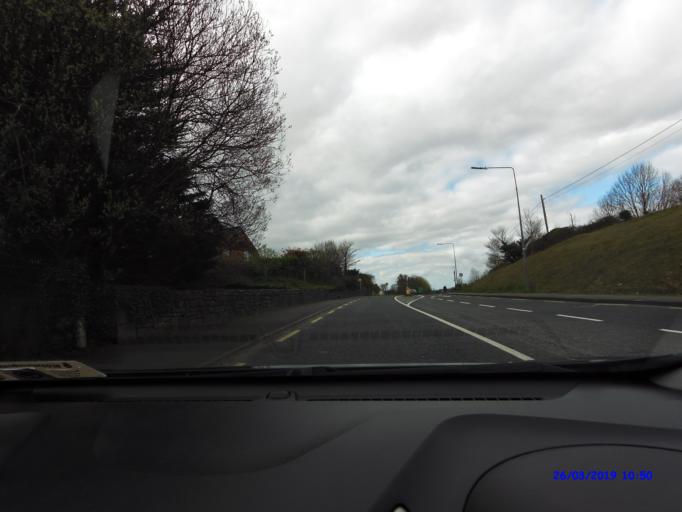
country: IE
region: Connaught
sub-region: Maigh Eo
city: Castlebar
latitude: 53.8498
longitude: -9.2847
